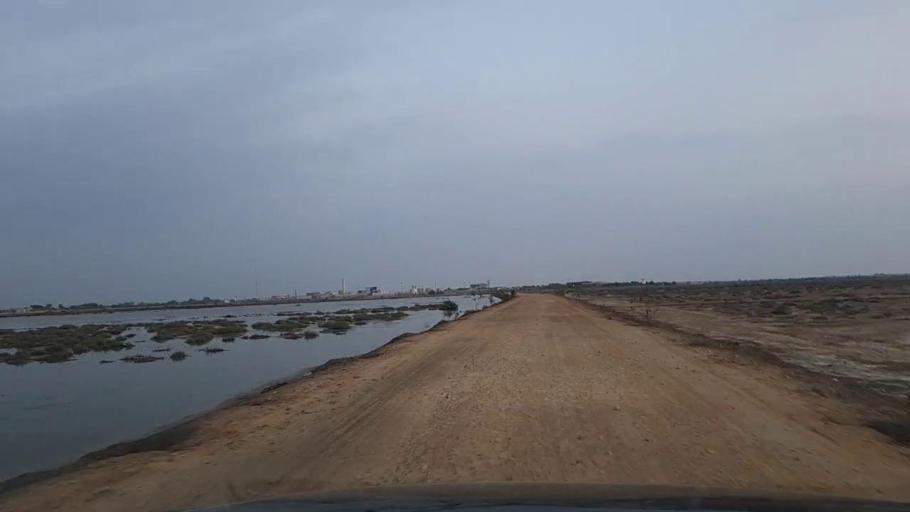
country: PK
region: Sindh
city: Jati
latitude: 24.4941
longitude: 68.3880
